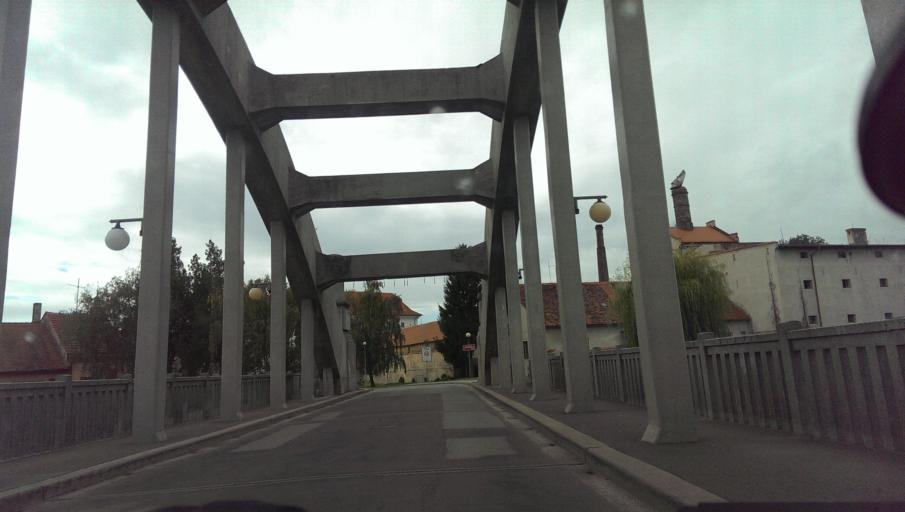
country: CZ
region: Zlin
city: Uhersky Ostroh
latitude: 48.9869
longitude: 17.3927
